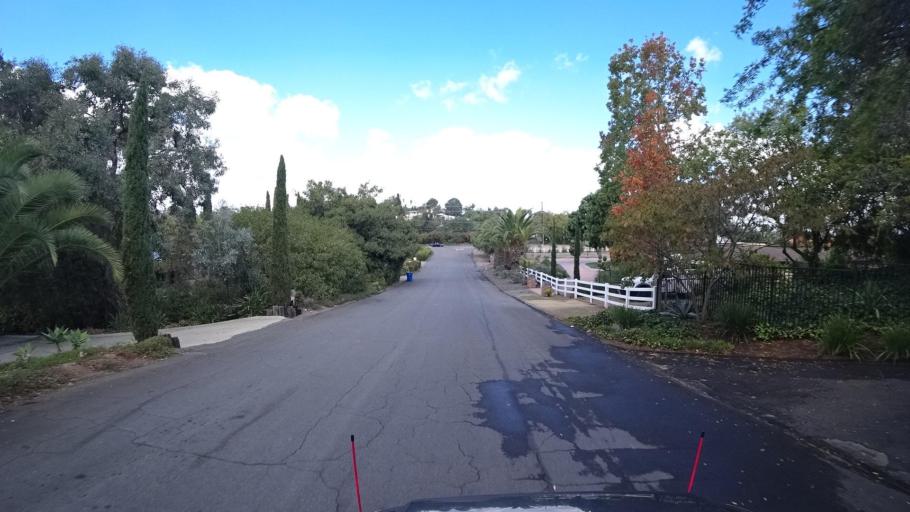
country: US
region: California
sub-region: San Diego County
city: Casa de Oro-Mount Helix
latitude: 32.7649
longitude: -116.9677
